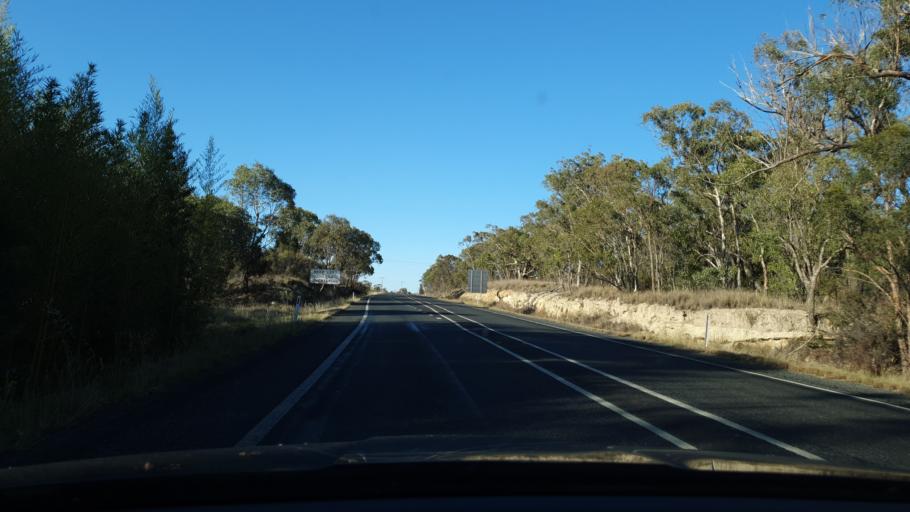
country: AU
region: Queensland
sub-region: Southern Downs
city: Stanthorpe
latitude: -28.6961
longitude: 151.9066
